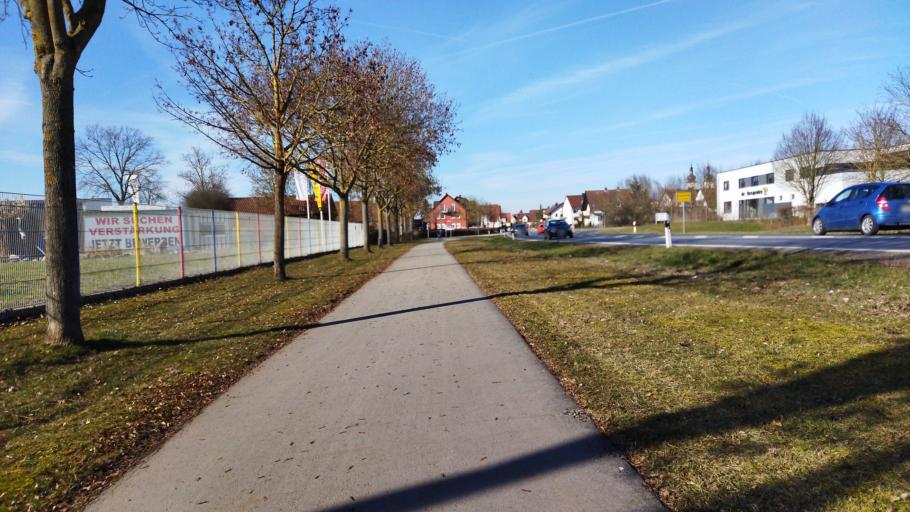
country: DE
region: Bavaria
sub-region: Regierungsbezirk Unterfranken
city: Grafenrheinfeld
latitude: 49.9950
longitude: 10.1987
